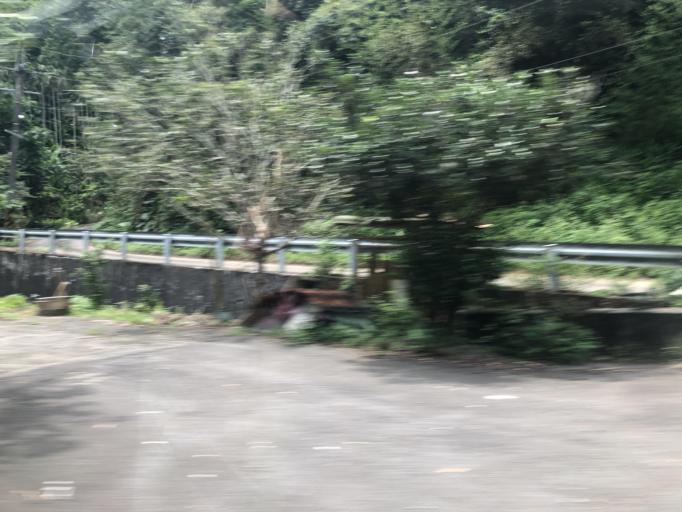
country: TW
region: Taipei
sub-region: Taipei
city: Banqiao
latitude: 24.9184
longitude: 121.4161
